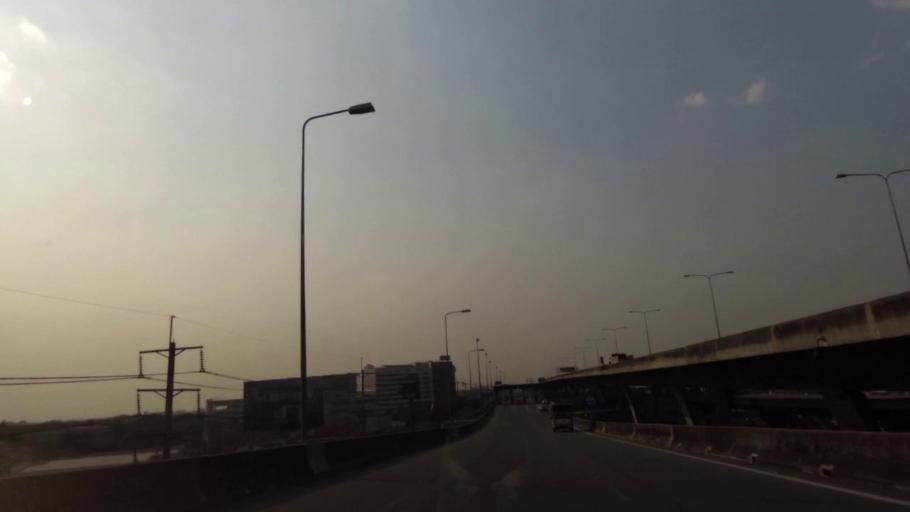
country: TH
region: Bangkok
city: Bang Na
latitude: 13.6286
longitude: 100.7201
